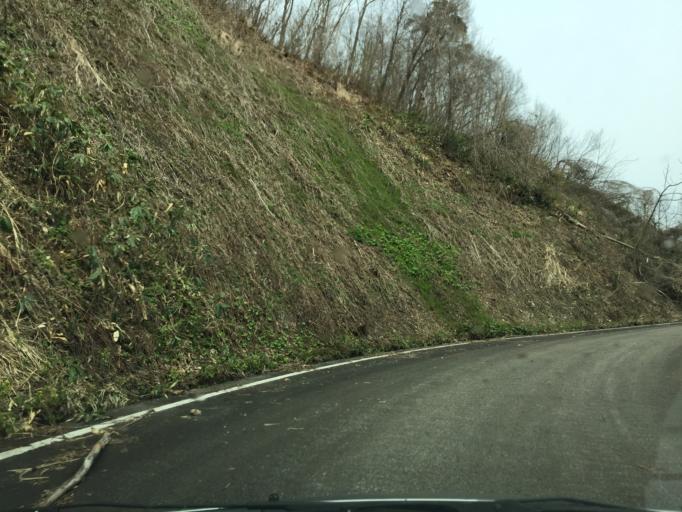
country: JP
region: Fukushima
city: Kitakata
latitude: 37.4768
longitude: 139.8022
